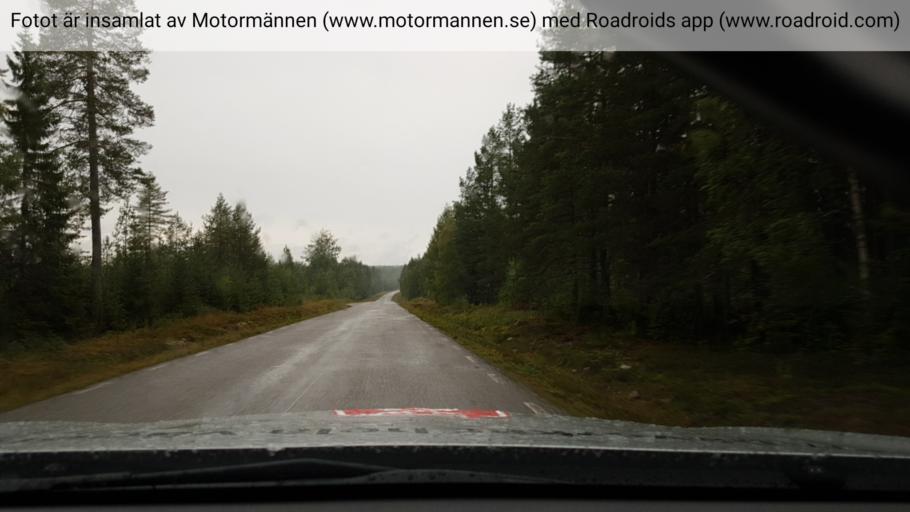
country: SE
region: Vaesterbotten
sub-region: Skelleftea Kommun
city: Burea
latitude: 64.3767
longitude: 21.2569
